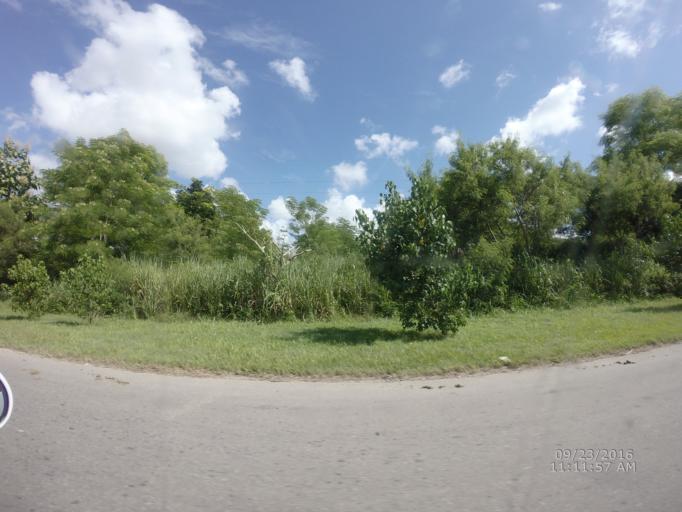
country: CU
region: La Habana
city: Arroyo Naranjo
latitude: 23.0274
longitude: -82.2765
